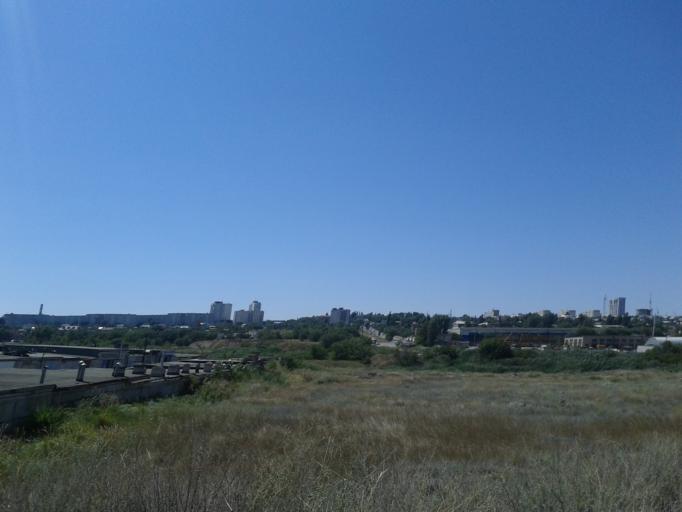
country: RU
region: Volgograd
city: Volgograd
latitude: 48.6892
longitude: 44.4500
